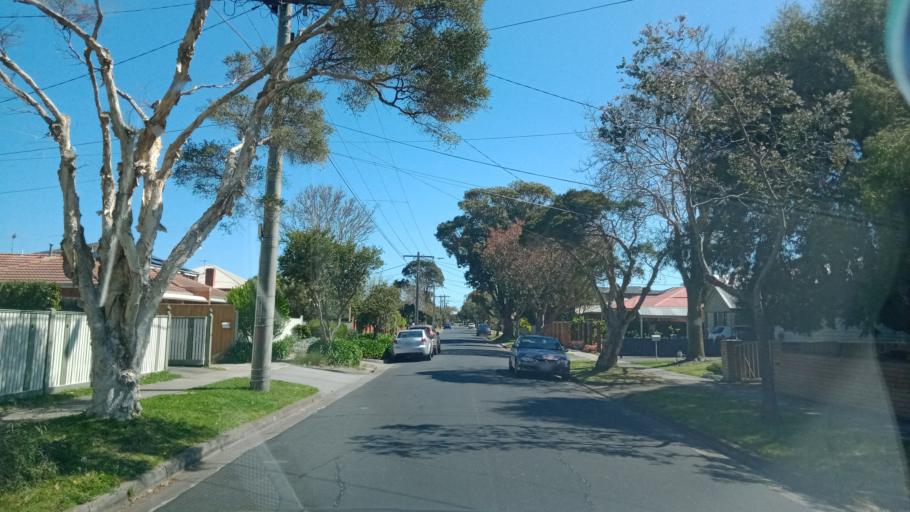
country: AU
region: Victoria
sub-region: Kingston
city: Chelsea
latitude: -38.0547
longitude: 145.1258
